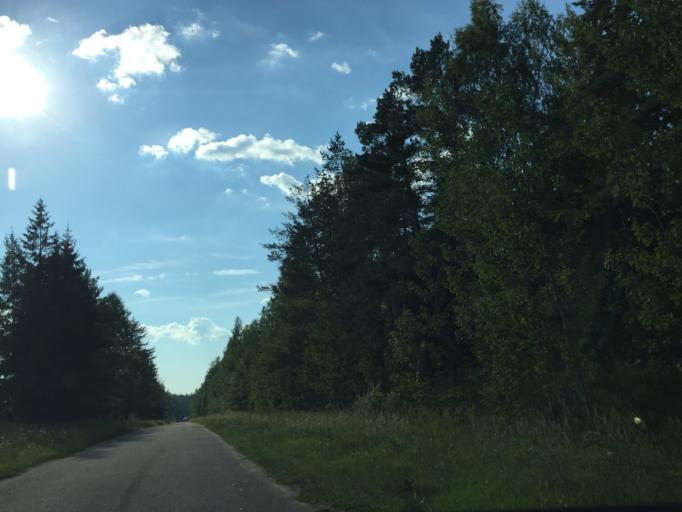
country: LV
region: Sigulda
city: Sigulda
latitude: 57.1347
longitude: 24.7814
